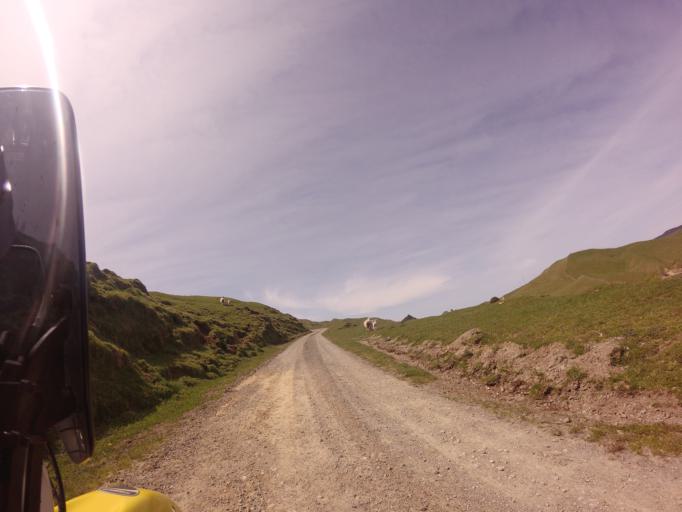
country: NZ
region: Bay of Plenty
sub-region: Opotiki District
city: Opotiki
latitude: -38.4534
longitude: 177.3654
